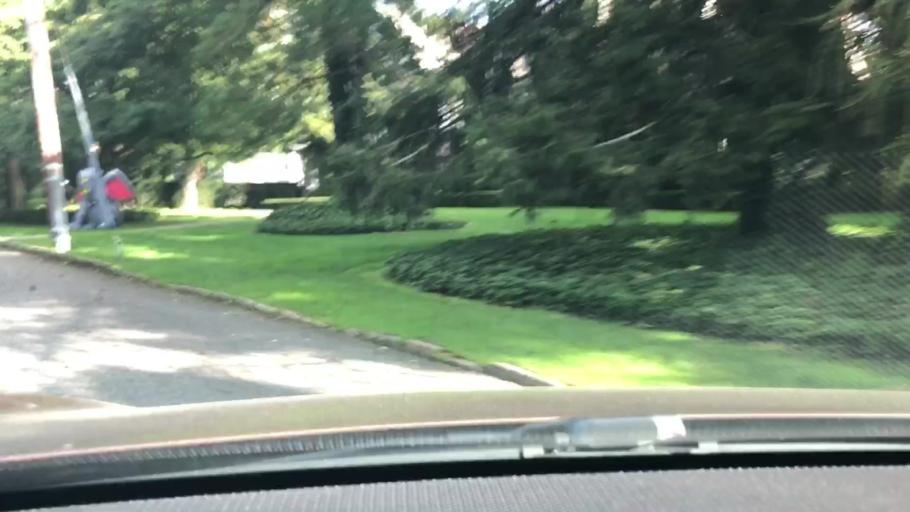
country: US
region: New York
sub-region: Westchester County
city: Bronxville
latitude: 40.9320
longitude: -73.8166
